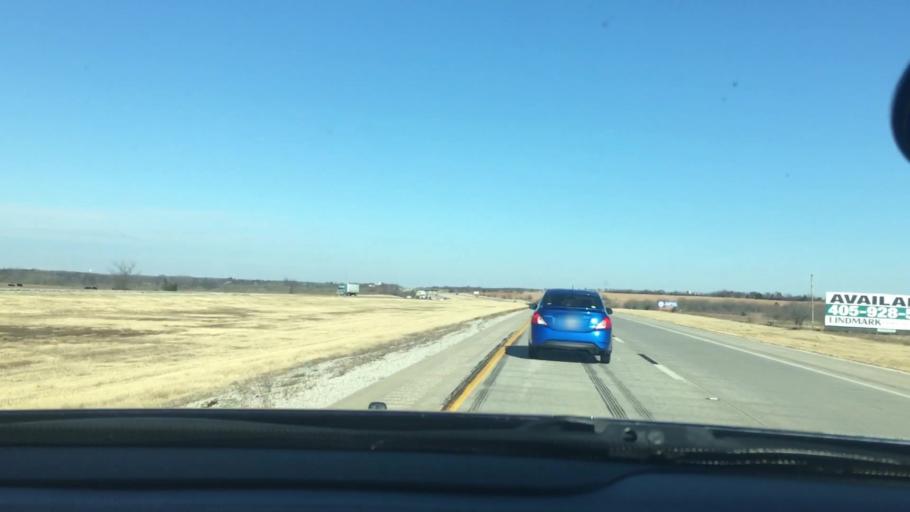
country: US
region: Oklahoma
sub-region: Carter County
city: Ardmore
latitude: 34.0988
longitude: -97.1511
